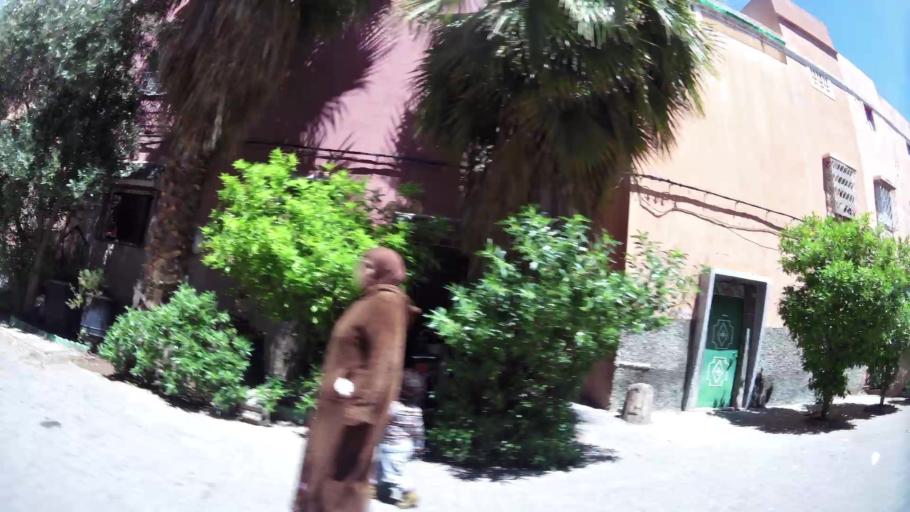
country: MA
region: Marrakech-Tensift-Al Haouz
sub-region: Marrakech
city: Marrakesh
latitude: 31.6293
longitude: -8.0438
